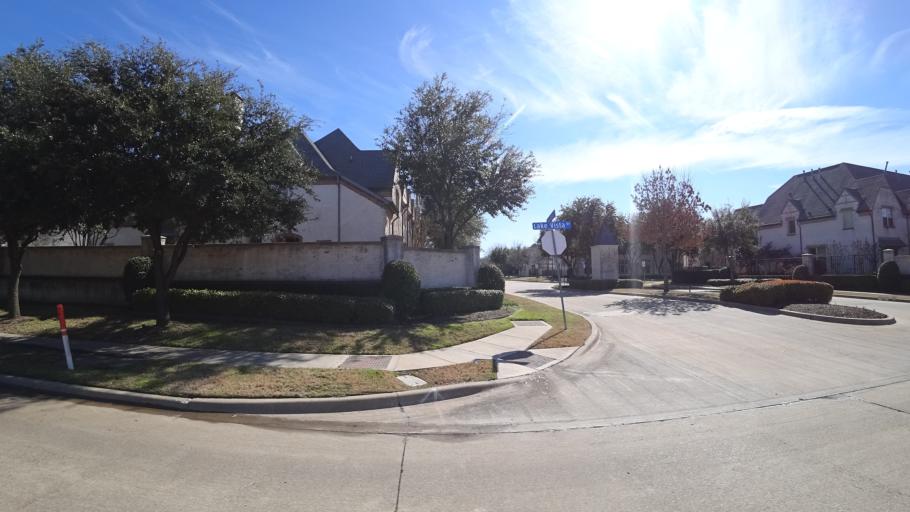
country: US
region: Texas
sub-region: Dallas County
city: Coppell
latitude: 32.9911
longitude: -96.9720
